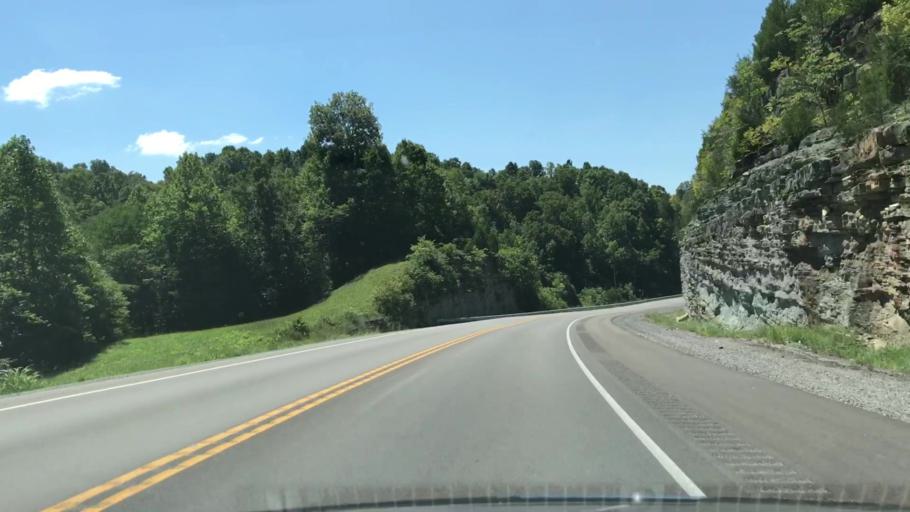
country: US
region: Kentucky
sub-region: Cumberland County
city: Burkesville
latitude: 36.7122
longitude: -85.3641
